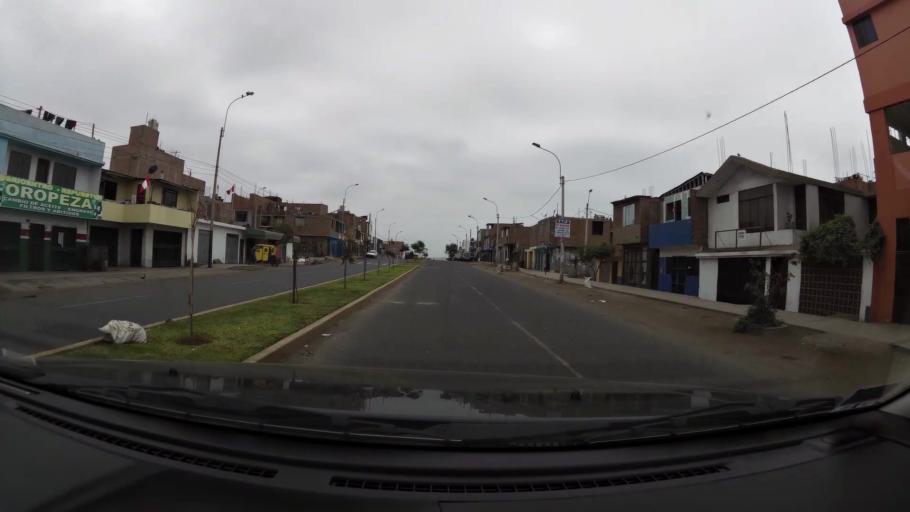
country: PE
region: Lima
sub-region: Lima
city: Surco
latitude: -12.1953
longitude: -76.9799
